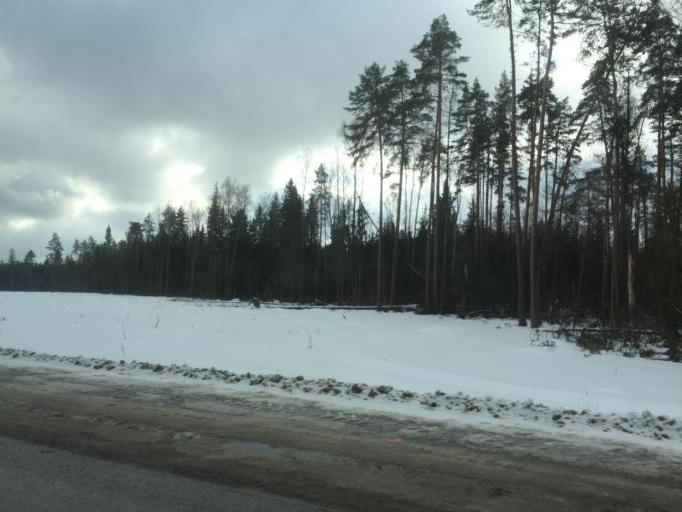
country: RU
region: Moskovskaya
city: Petrovo-Dal'neye
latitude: 55.7956
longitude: 37.1466
